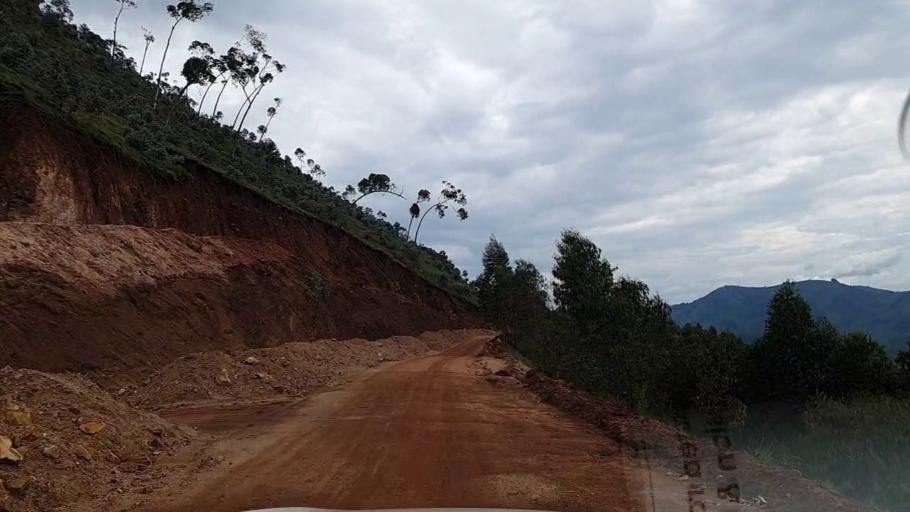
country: RW
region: Southern Province
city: Nzega
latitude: -2.3709
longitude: 29.4497
